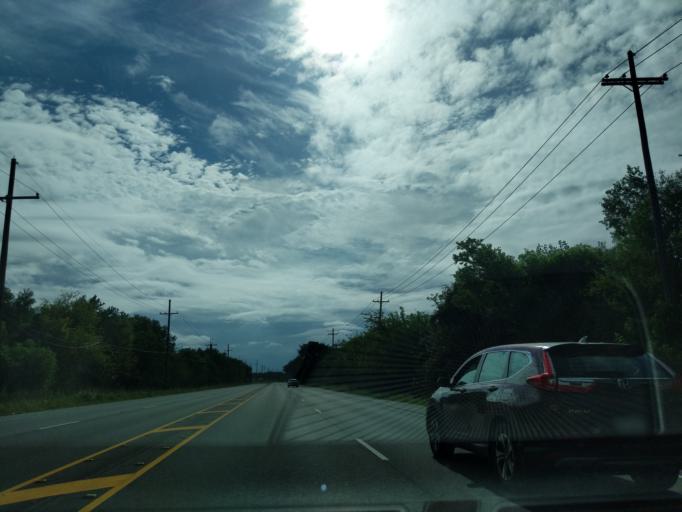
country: US
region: Louisiana
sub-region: Saint Bernard Parish
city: Meraux
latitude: 30.0590
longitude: -89.8698
